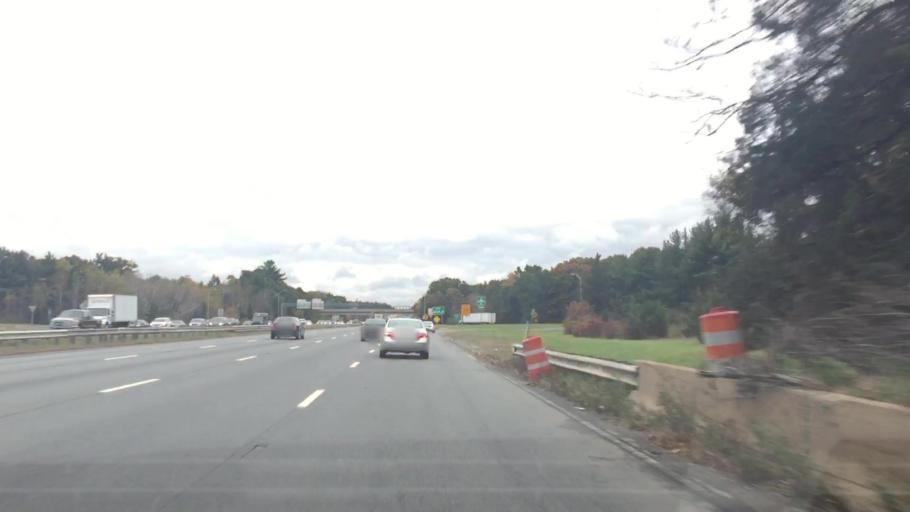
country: US
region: Massachusetts
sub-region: Essex County
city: Lawrence
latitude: 42.6713
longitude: -71.1978
